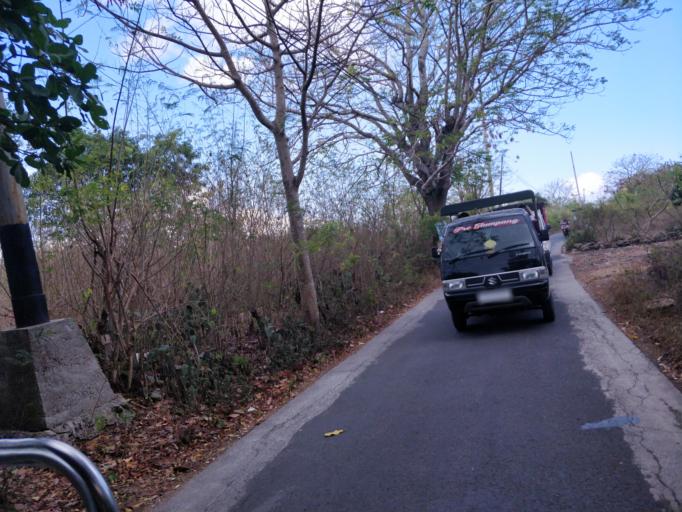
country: ID
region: Bali
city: Jungutbatu Kaja Dua
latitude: -8.6821
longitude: 115.4457
